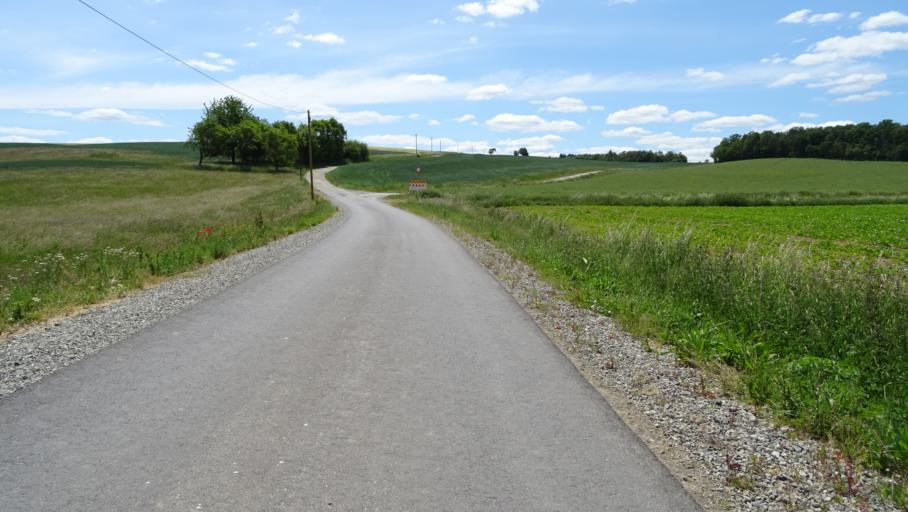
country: DE
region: Baden-Wuerttemberg
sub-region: Karlsruhe Region
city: Buchen
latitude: 49.4878
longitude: 9.3369
